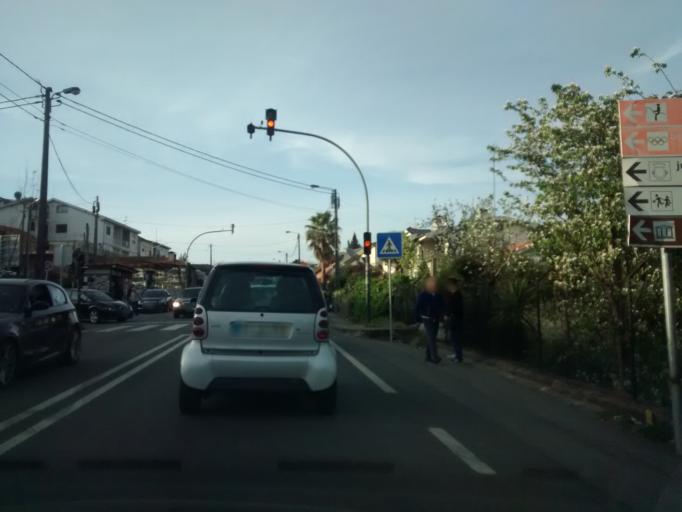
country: PT
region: Braga
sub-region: Guimaraes
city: Guimaraes
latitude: 41.4579
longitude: -8.3117
